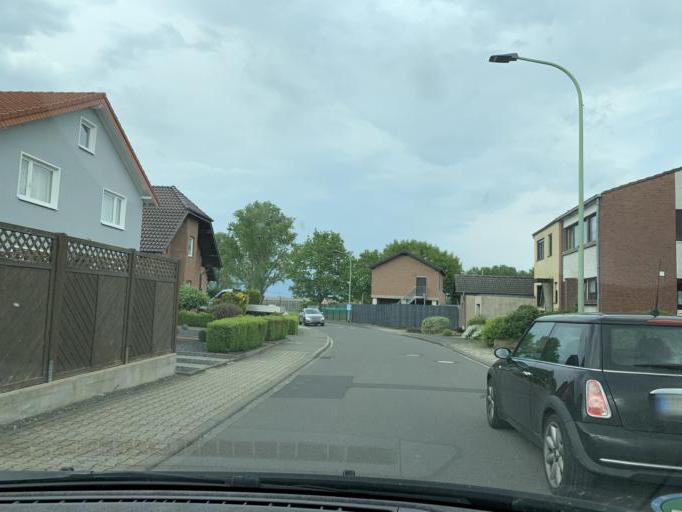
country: DE
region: North Rhine-Westphalia
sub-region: Regierungsbezirk Koln
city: Kreuzau
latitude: 50.7584
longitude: 6.5245
